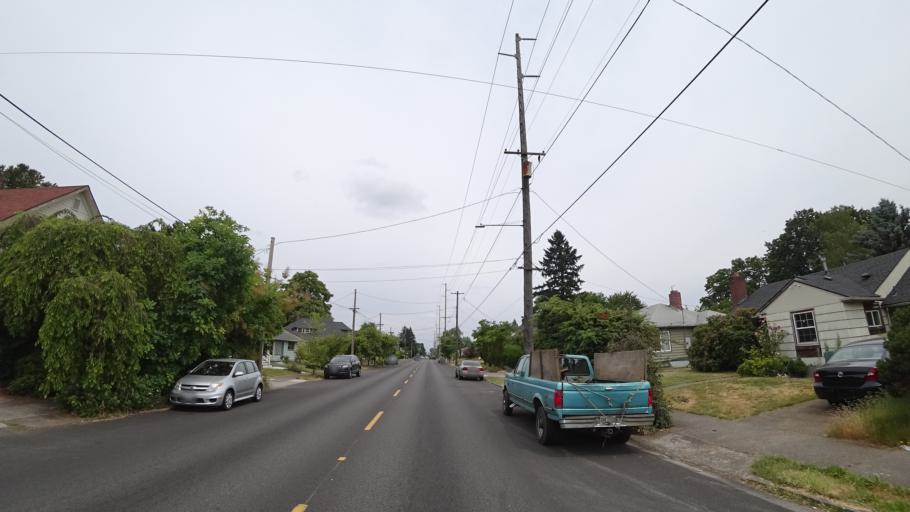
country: US
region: Oregon
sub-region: Multnomah County
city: Portland
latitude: 45.5668
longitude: -122.6956
